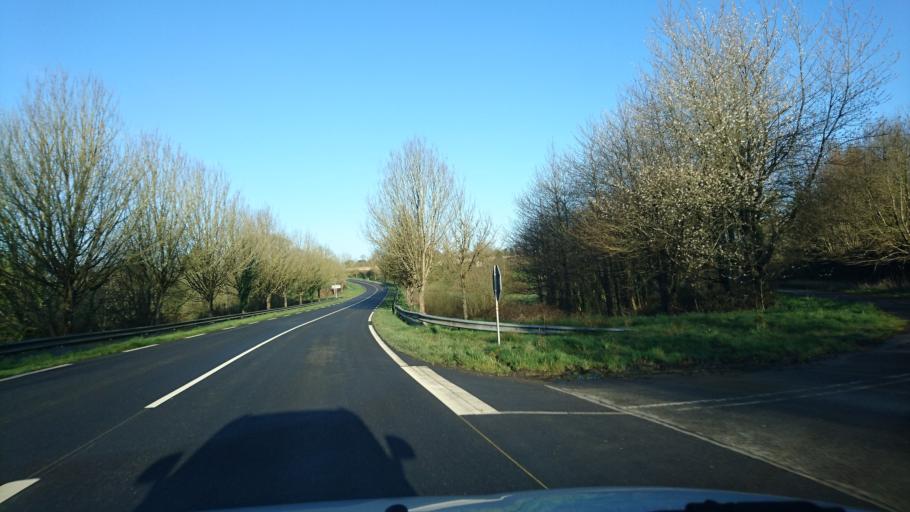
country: FR
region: Brittany
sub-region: Departement d'Ille-et-Vilaine
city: Pleine-Fougeres
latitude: 48.4952
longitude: -1.5978
